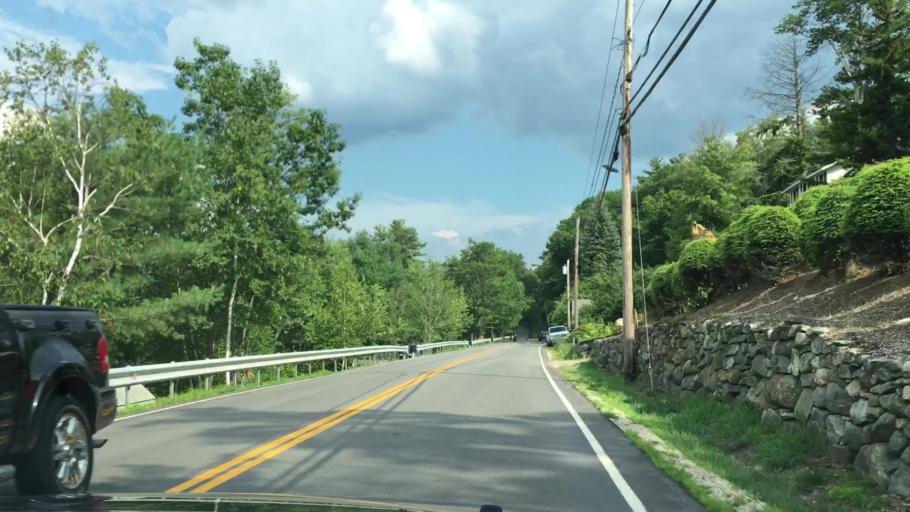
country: US
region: New Hampshire
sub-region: Belknap County
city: Gilford
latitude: 43.5609
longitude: -71.3318
